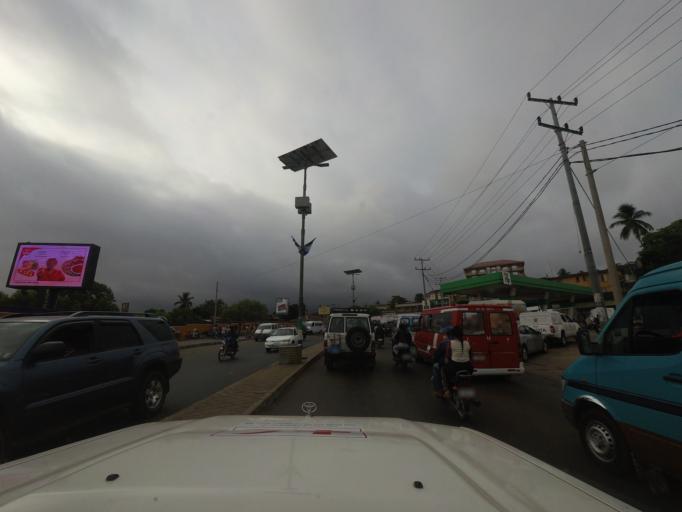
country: SL
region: Western Area
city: Freetown
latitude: 8.4841
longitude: -13.2593
